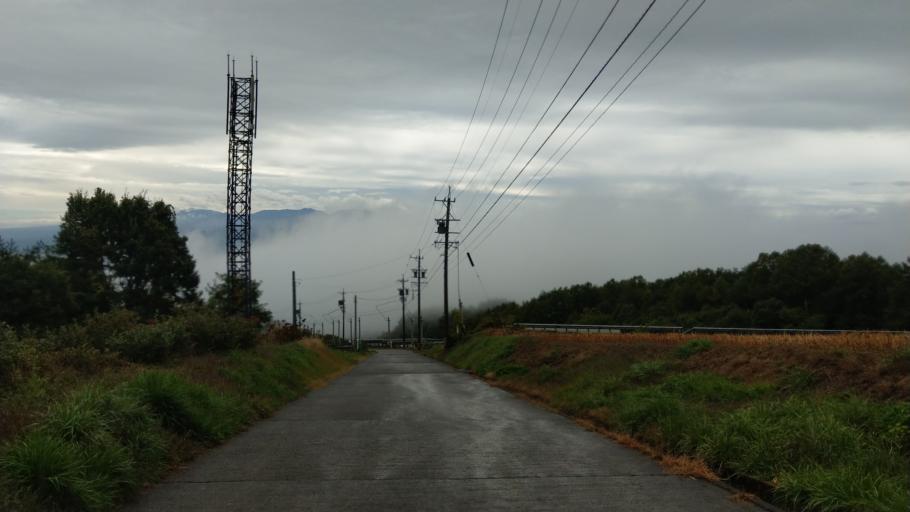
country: JP
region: Nagano
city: Komoro
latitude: 36.3625
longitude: 138.4259
